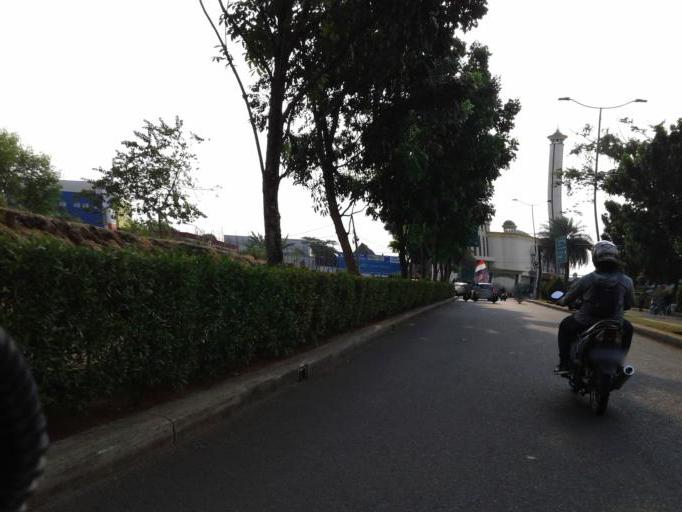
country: ID
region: Banten
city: South Tangerang
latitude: -6.2854
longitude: 106.7268
